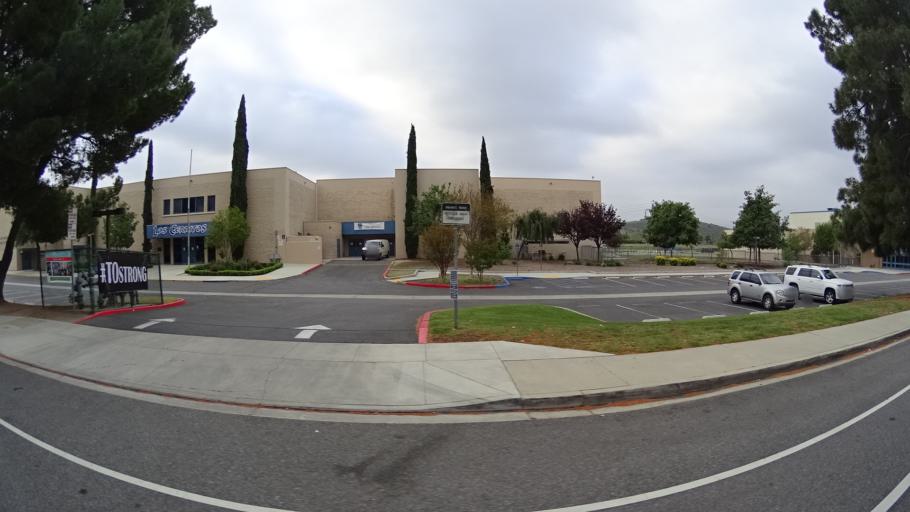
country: US
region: California
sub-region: Ventura County
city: Thousand Oaks
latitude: 34.2078
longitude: -118.8406
